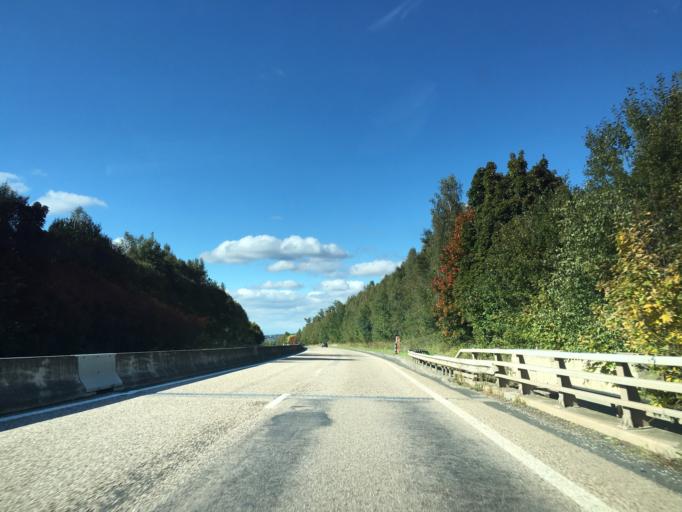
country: FR
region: Lorraine
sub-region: Departement de Meurthe-et-Moselle
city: Baccarat
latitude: 48.4621
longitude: 6.7466
